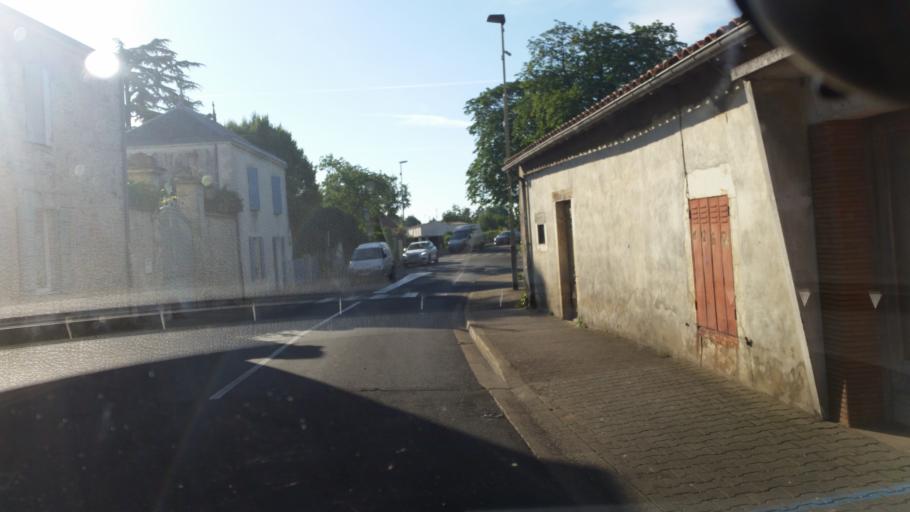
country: FR
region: Poitou-Charentes
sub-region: Departement de la Charente-Maritime
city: Perigny
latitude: 46.1675
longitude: -1.1098
